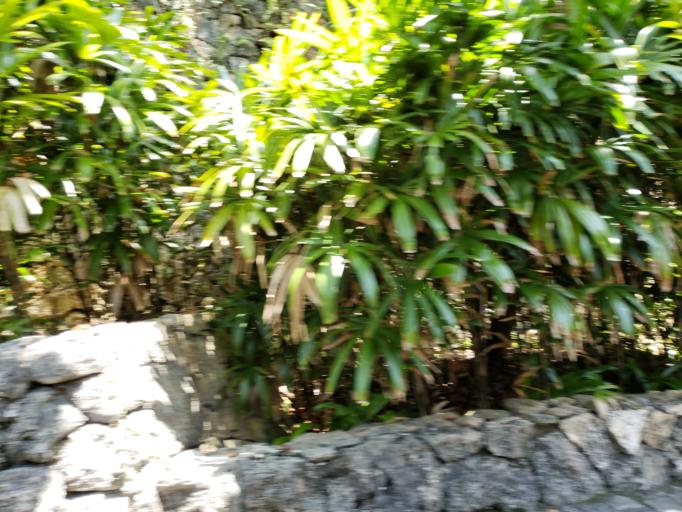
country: ID
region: Bali
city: Pecatu
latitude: -8.8444
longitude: 115.1215
